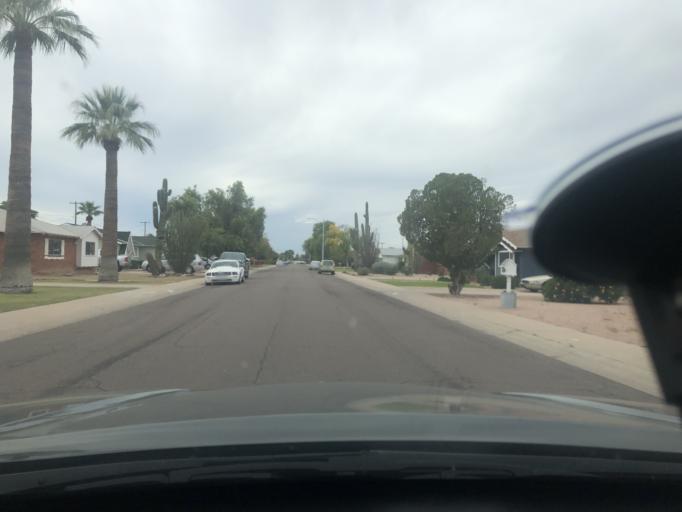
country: US
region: Arizona
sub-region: Maricopa County
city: Scottsdale
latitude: 33.4920
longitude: -111.9017
